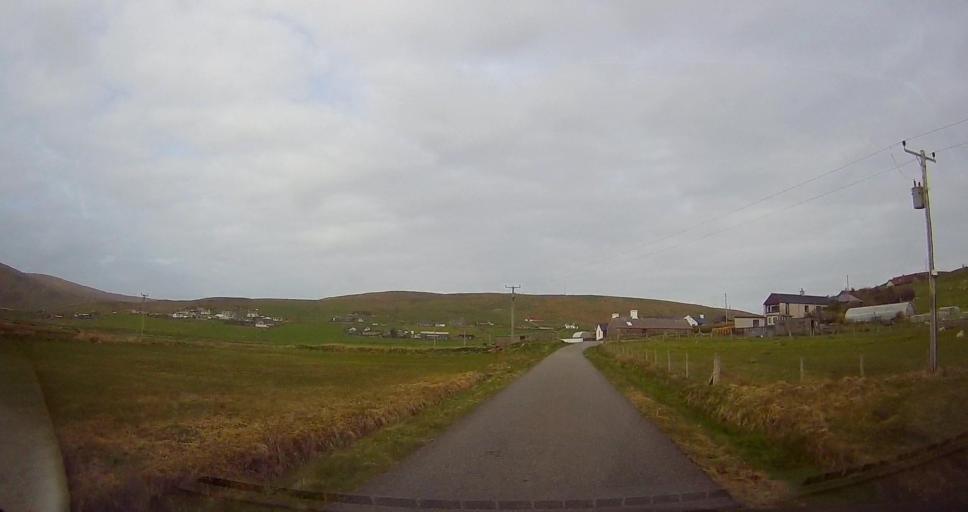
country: GB
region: Scotland
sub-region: Shetland Islands
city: Sandwick
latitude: 60.0471
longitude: -1.2130
